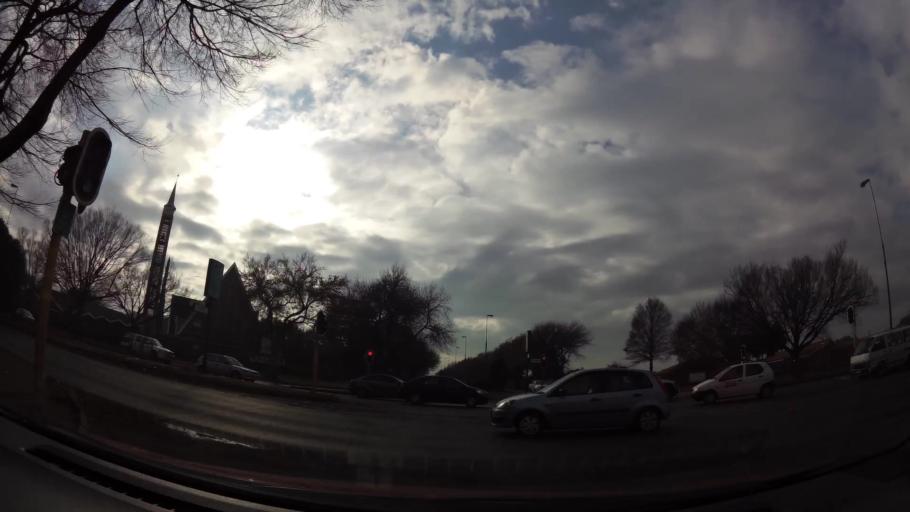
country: ZA
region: Gauteng
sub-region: Sedibeng District Municipality
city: Vanderbijlpark
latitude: -26.7055
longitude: 27.8240
